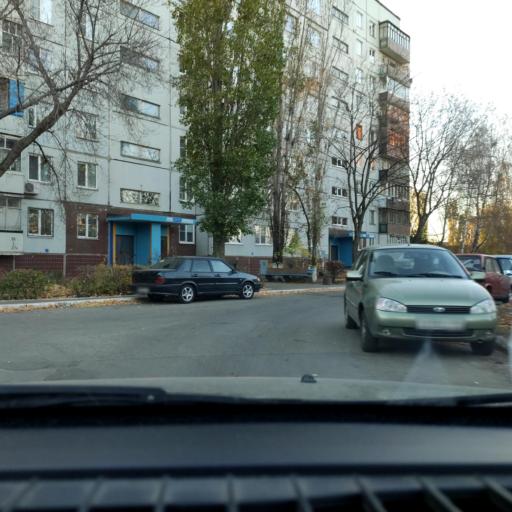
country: RU
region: Samara
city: Tol'yatti
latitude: 53.5397
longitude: 49.3171
